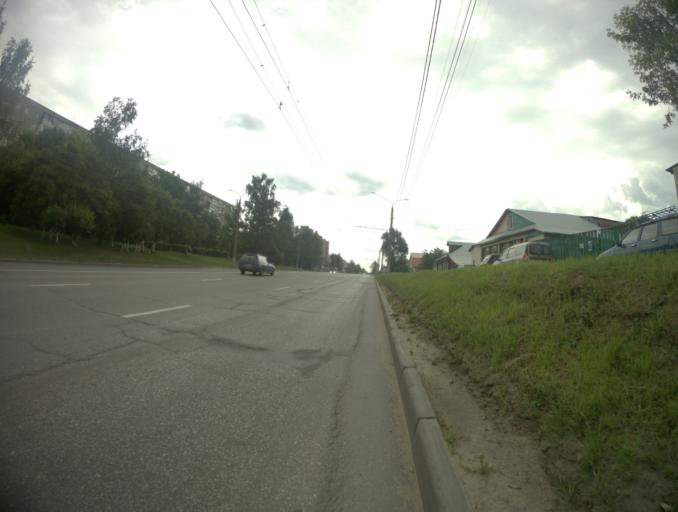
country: RU
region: Vladimir
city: Kommunar
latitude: 56.1574
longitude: 40.4659
